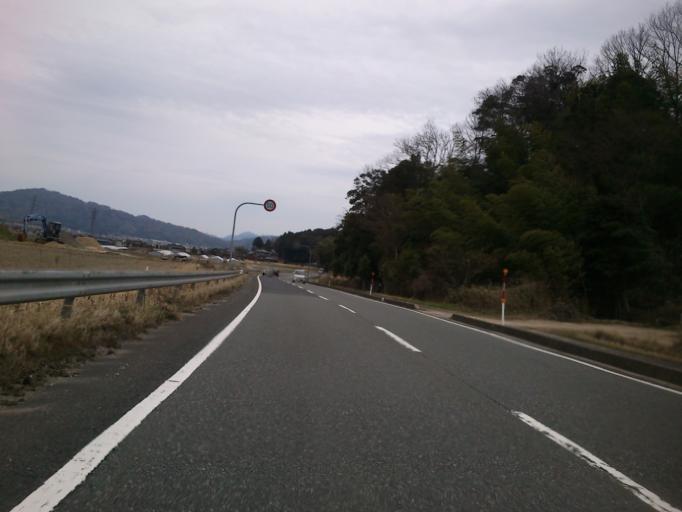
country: JP
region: Kyoto
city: Miyazu
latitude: 35.4911
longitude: 135.0990
